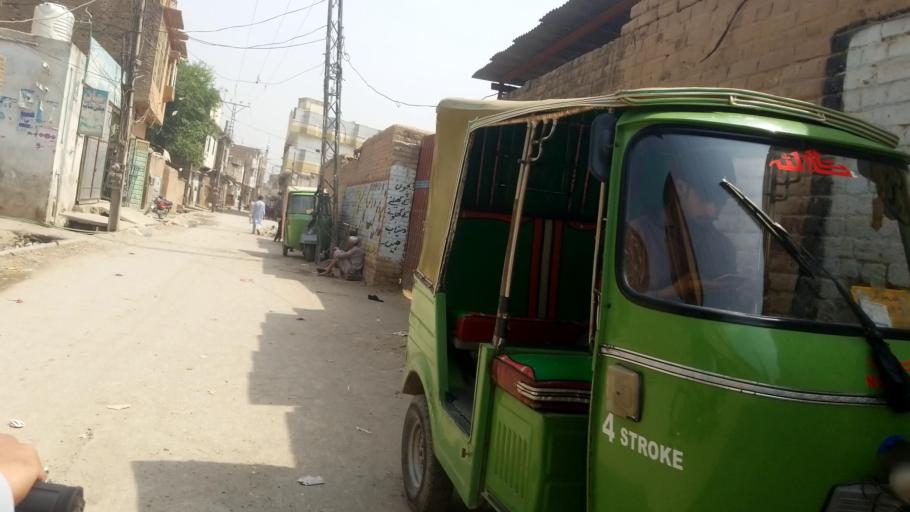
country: PK
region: Khyber Pakhtunkhwa
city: Peshawar
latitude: 33.9867
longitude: 71.5405
